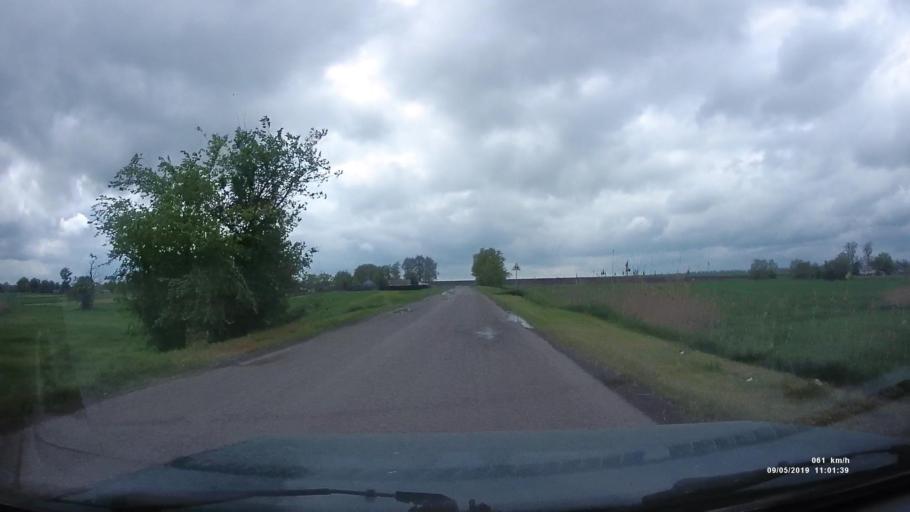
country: RU
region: Rostov
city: Peshkovo
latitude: 46.8442
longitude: 39.2126
